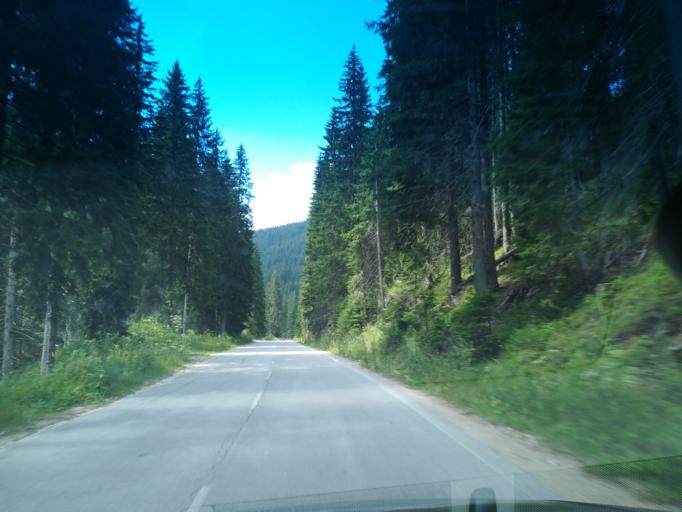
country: BG
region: Smolyan
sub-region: Obshtina Chepelare
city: Chepelare
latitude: 41.6595
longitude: 24.6821
